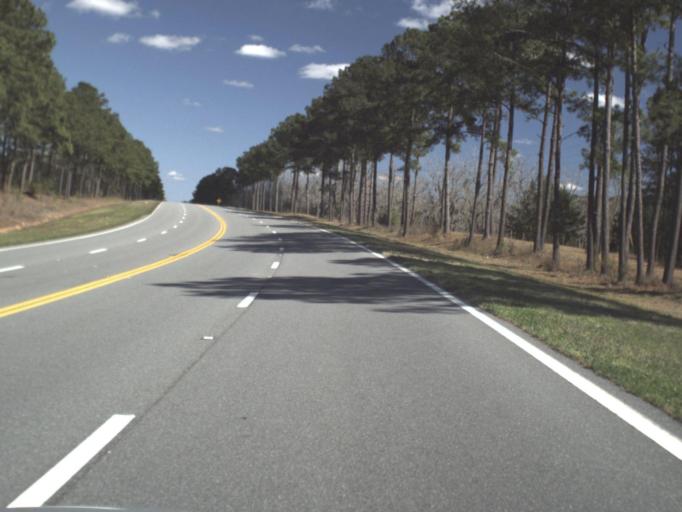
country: US
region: Florida
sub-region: Gadsden County
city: Chattahoochee
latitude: 30.7003
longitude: -84.8094
